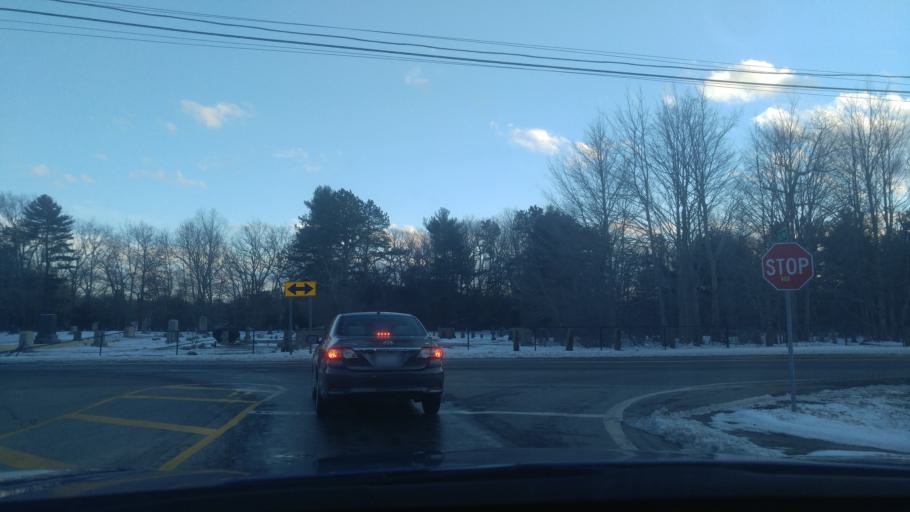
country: US
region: Rhode Island
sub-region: Kent County
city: West Greenwich
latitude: 41.6691
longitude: -71.6047
